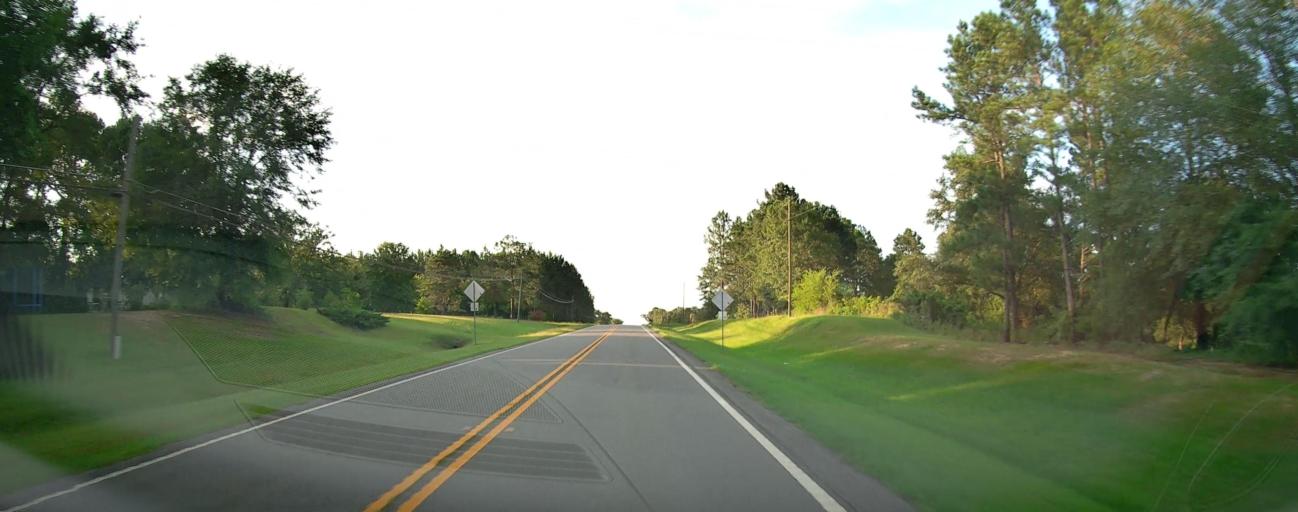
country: US
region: Georgia
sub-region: Taylor County
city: Reynolds
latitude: 32.5783
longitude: -84.0898
